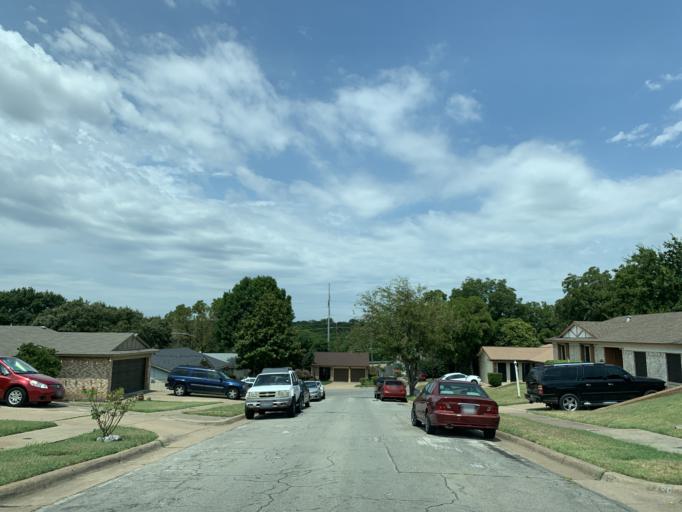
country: US
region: Texas
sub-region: Dallas County
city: DeSoto
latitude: 32.6611
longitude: -96.8131
